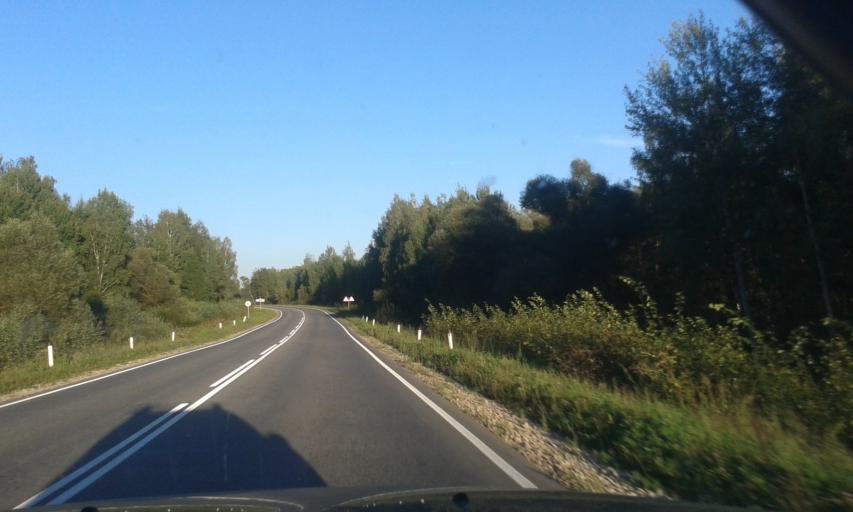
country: RU
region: Tula
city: Krapivna
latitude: 54.1129
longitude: 37.2003
